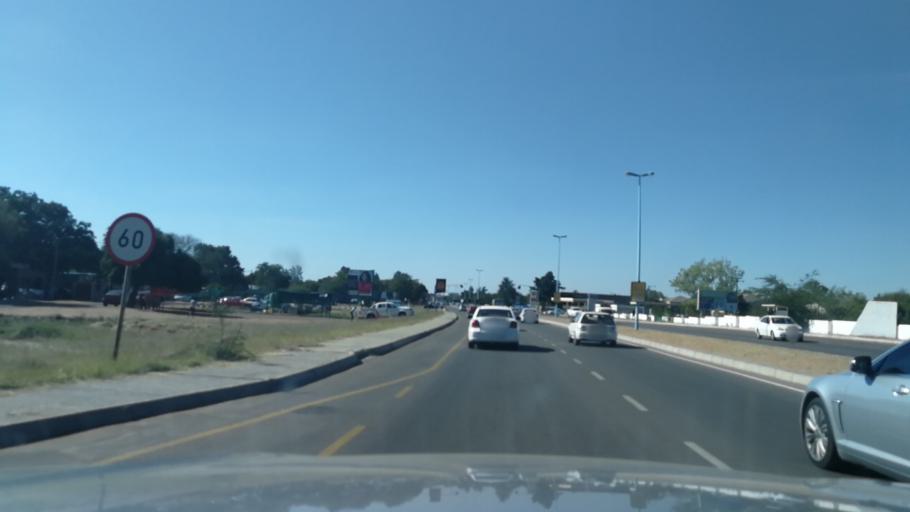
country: BW
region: South East
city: Gaborone
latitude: -24.6788
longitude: 25.9182
